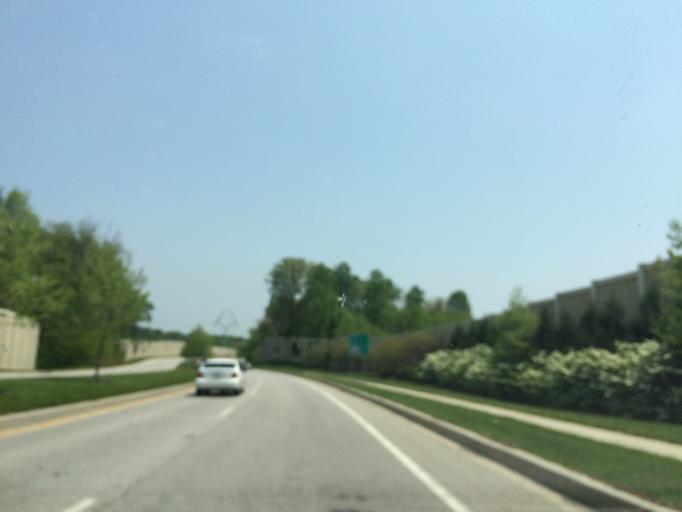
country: US
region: Maryland
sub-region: Howard County
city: North Laurel
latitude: 39.1444
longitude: -76.8946
